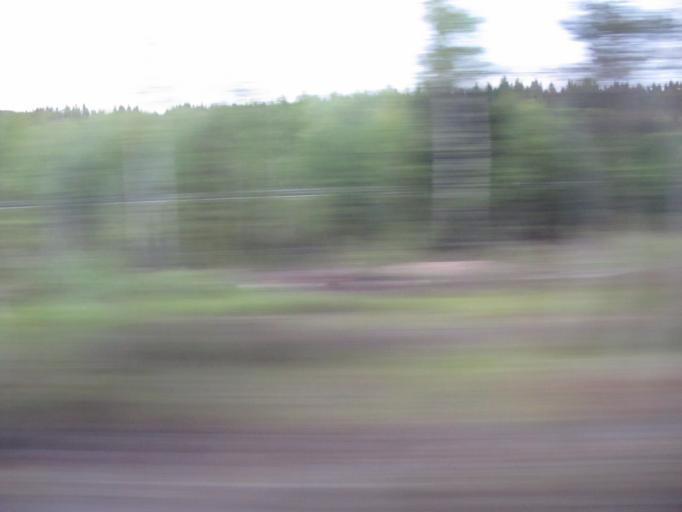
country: NO
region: Oppland
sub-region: Lillehammer
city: Lillehammer
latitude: 61.2055
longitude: 10.4248
